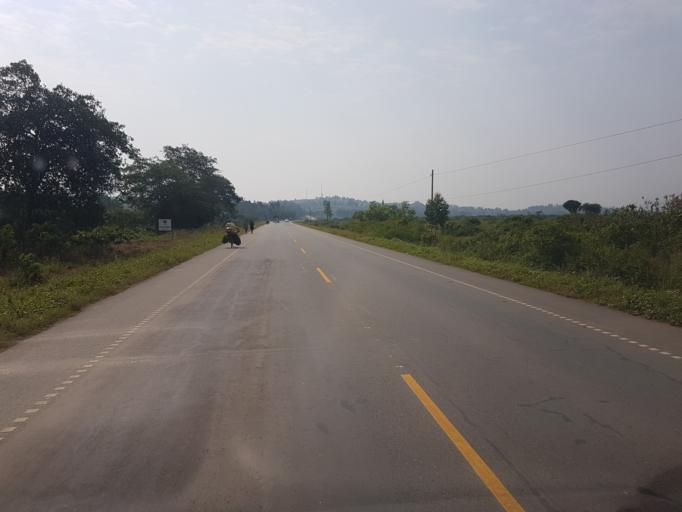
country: UG
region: Western Region
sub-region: Mbarara District
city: Bwizibwera
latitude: -0.6424
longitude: 30.5757
